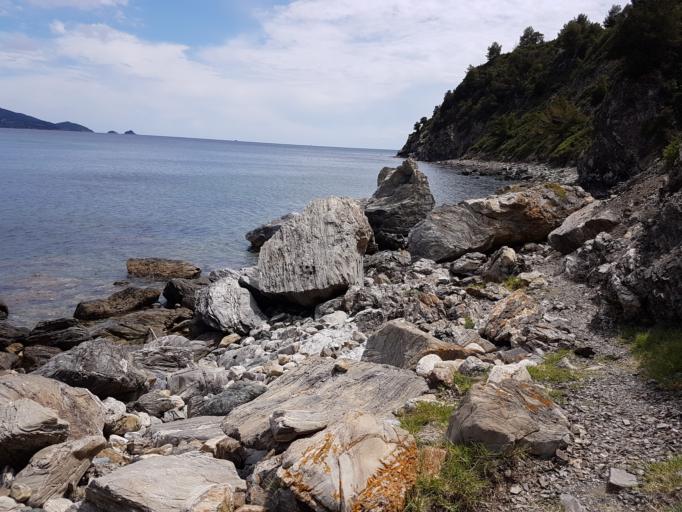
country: IT
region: Tuscany
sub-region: Provincia di Livorno
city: Capoliveri
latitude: 42.7627
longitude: 10.3328
